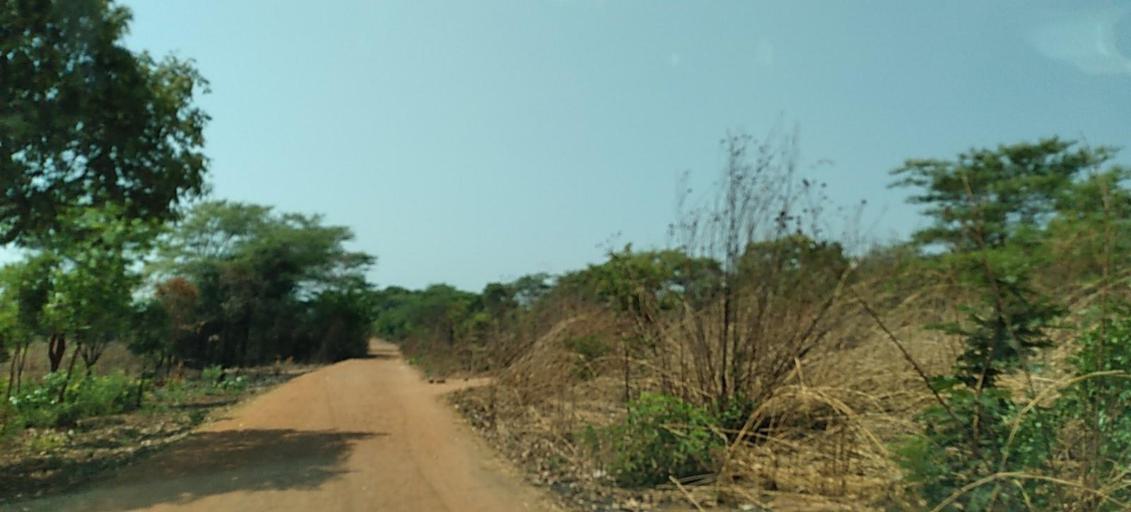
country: ZM
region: Copperbelt
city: Luanshya
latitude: -13.3433
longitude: 28.3922
